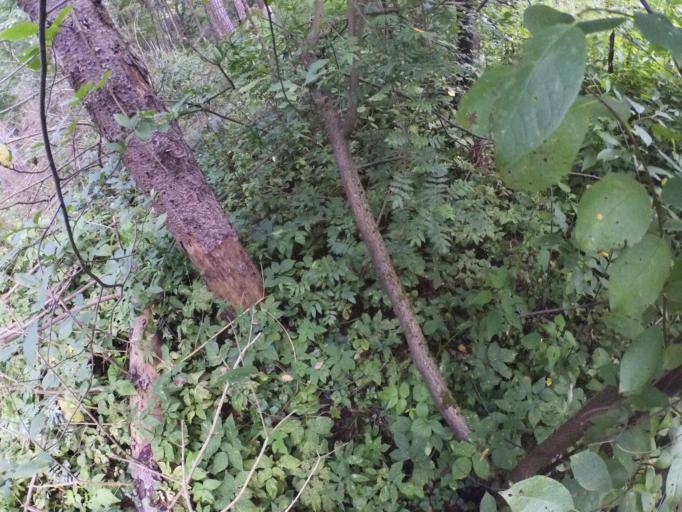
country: RU
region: Moskovskaya
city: Fosforitnyy
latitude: 55.3386
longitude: 38.9396
